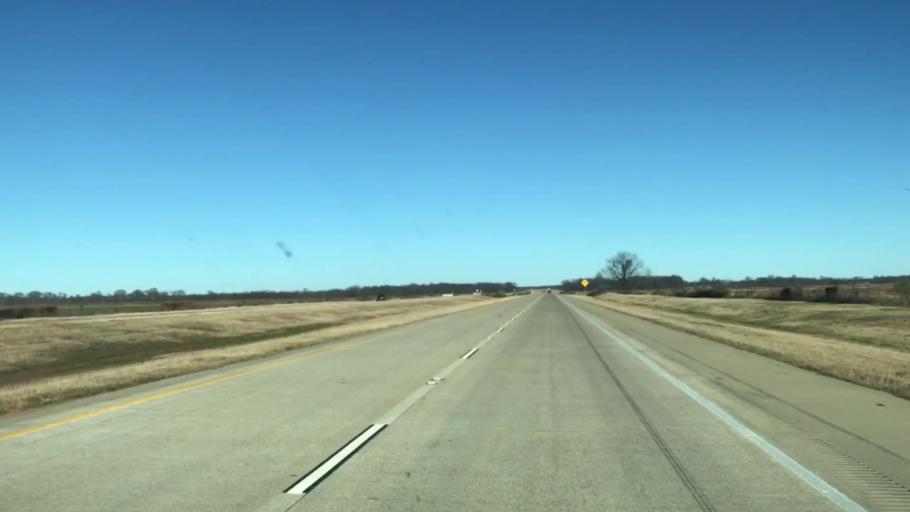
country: US
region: Louisiana
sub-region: Caddo Parish
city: Oil City
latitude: 32.7280
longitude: -93.8721
